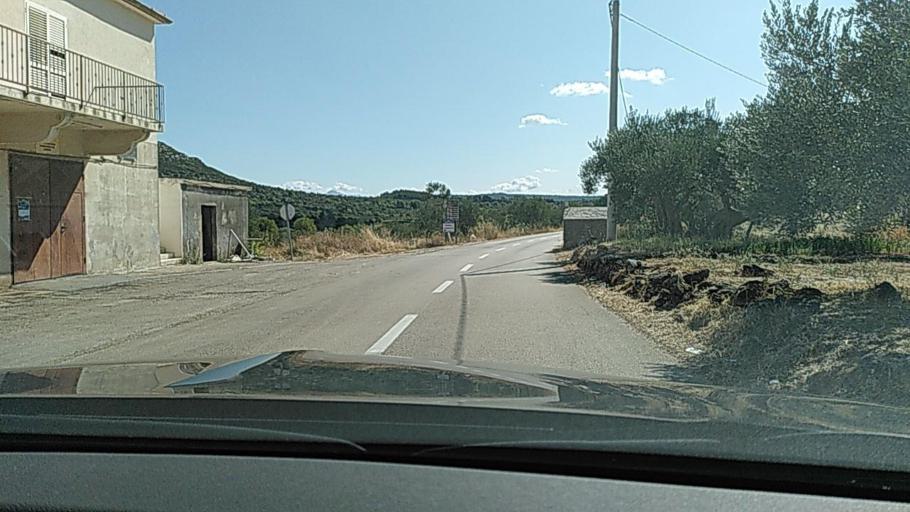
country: HR
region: Splitsko-Dalmatinska
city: Jelsa
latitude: 43.1442
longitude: 16.8413
